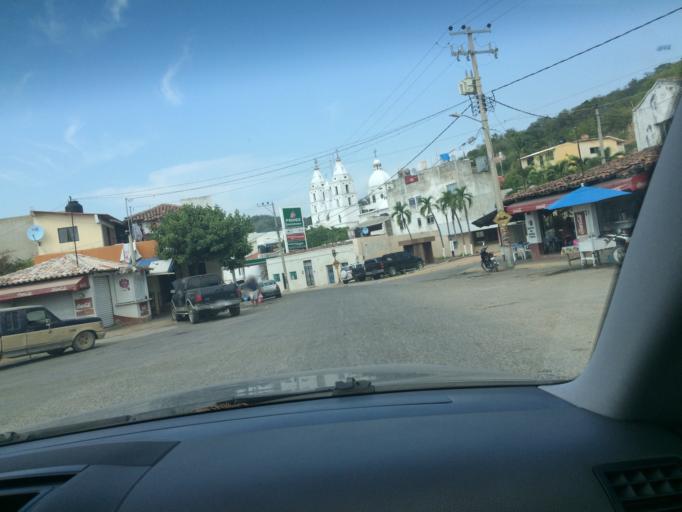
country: MX
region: Jalisco
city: Cihuatlan
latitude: 19.2377
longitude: -104.5558
